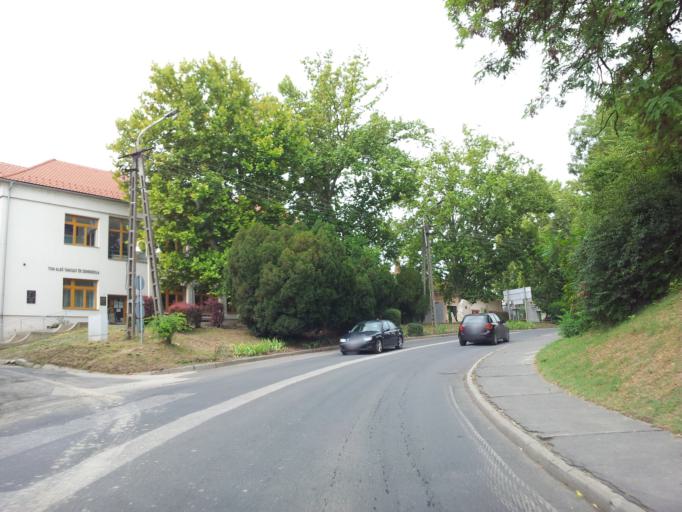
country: HU
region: Tolna
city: Tamasi
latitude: 46.6308
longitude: 18.2826
